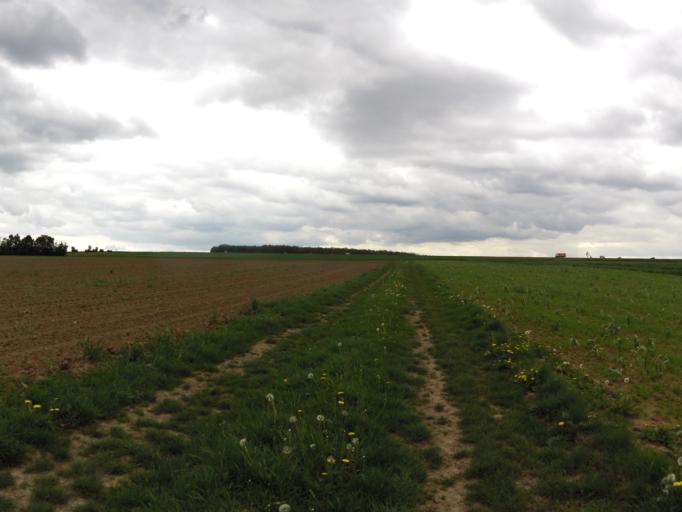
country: DE
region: Bavaria
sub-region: Regierungsbezirk Unterfranken
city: Unterpleichfeld
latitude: 49.8557
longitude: 10.0648
